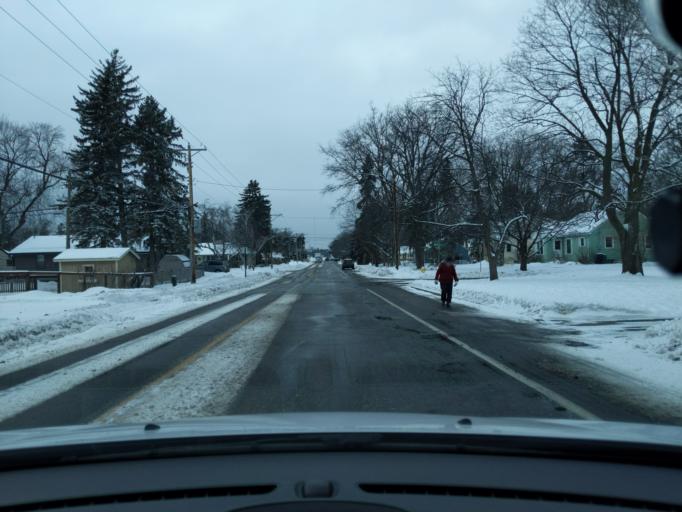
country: US
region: Minnesota
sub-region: Ramsey County
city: Falcon Heights
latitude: 44.9990
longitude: -93.1631
